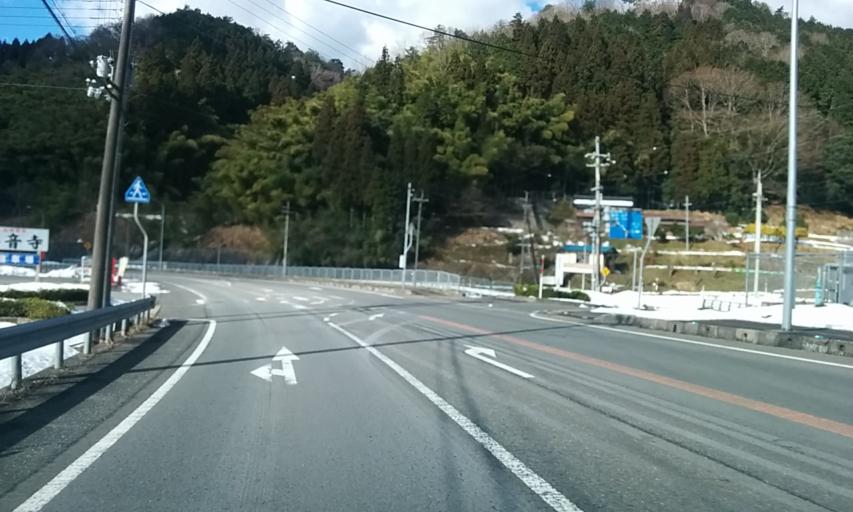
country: JP
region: Kyoto
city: Fukuchiyama
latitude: 35.4217
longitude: 135.0286
